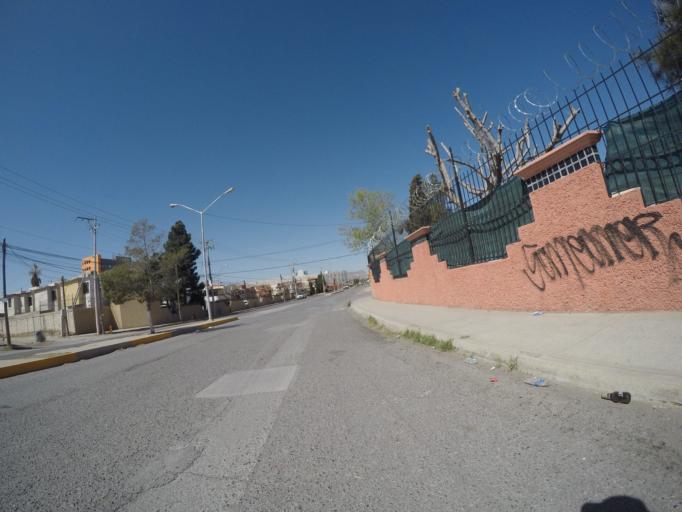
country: MX
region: Chihuahua
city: Ciudad Juarez
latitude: 31.6922
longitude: -106.4209
